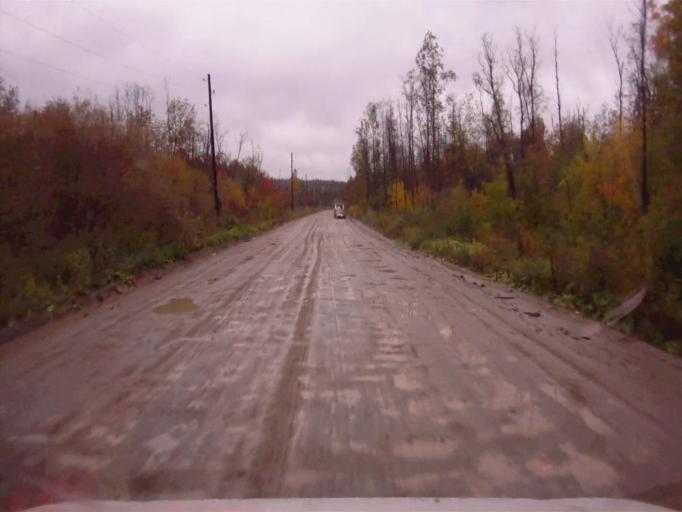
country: RU
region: Chelyabinsk
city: Kyshtym
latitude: 55.7367
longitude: 60.5139
